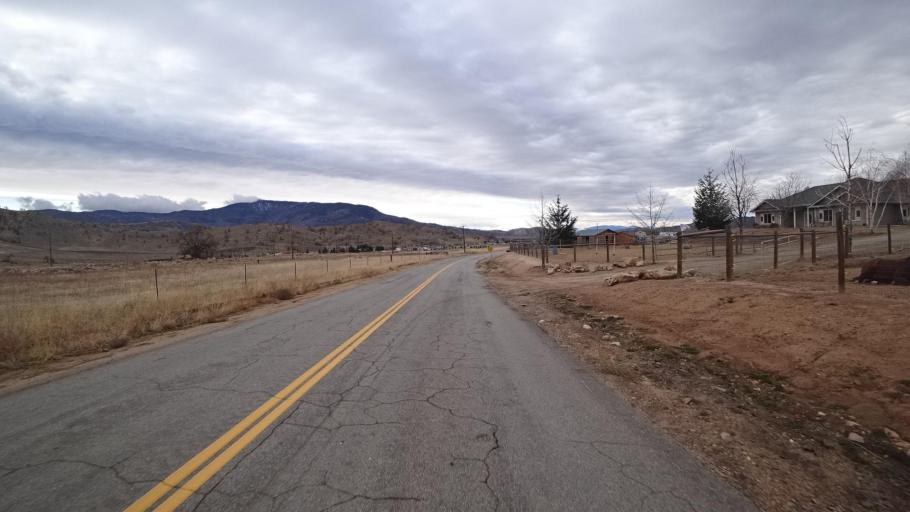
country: US
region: California
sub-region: Kern County
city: Bear Valley Springs
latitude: 35.1322
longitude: -118.5649
